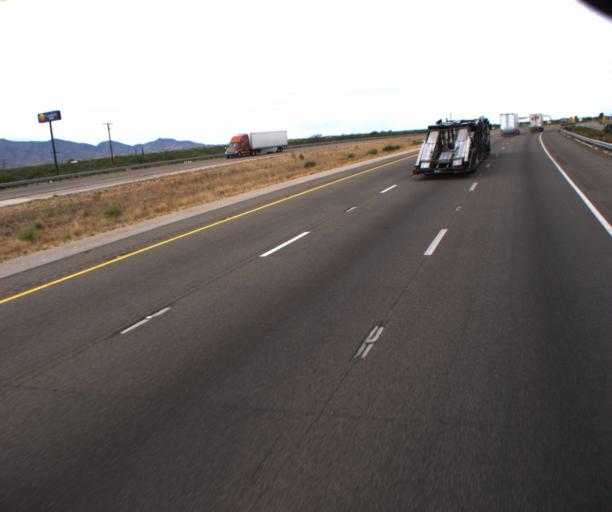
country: US
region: Arizona
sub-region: Cochise County
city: Whetstone
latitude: 31.9645
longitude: -110.3480
